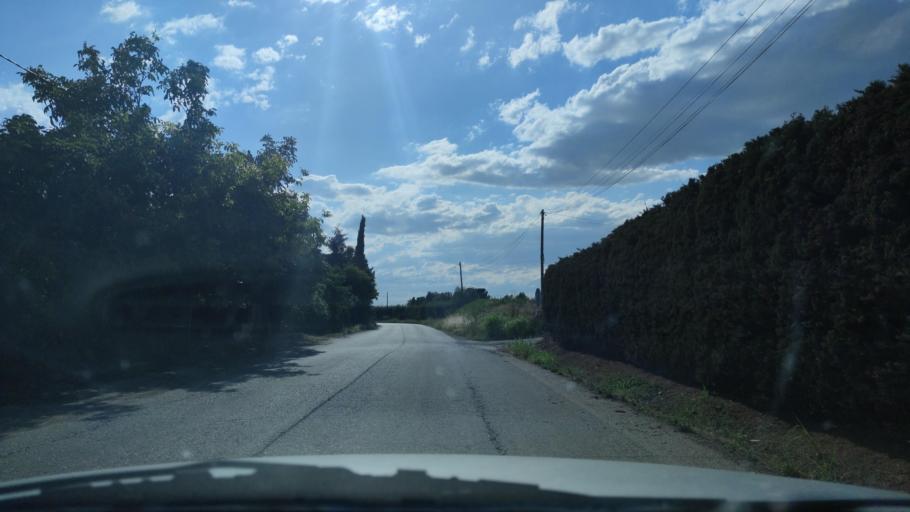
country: ES
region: Catalonia
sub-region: Provincia de Lleida
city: Alpicat
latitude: 41.6241
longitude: 0.5658
